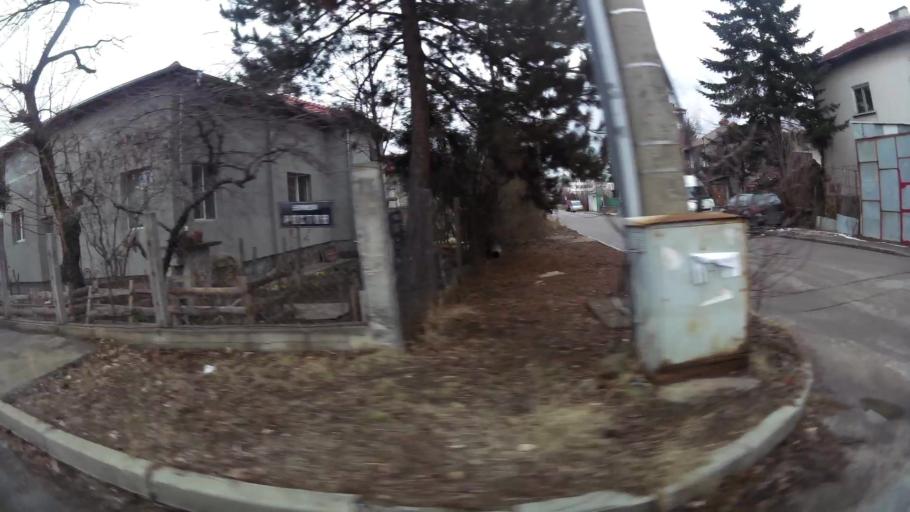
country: BG
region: Sofia-Capital
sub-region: Stolichna Obshtina
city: Sofia
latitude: 42.7249
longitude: 23.2681
